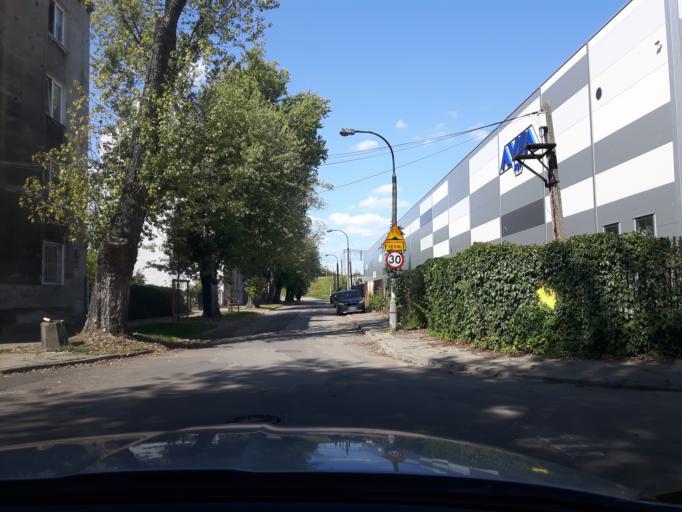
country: PL
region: Masovian Voivodeship
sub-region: Warszawa
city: Praga Polnoc
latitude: 52.2607
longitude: 21.0601
